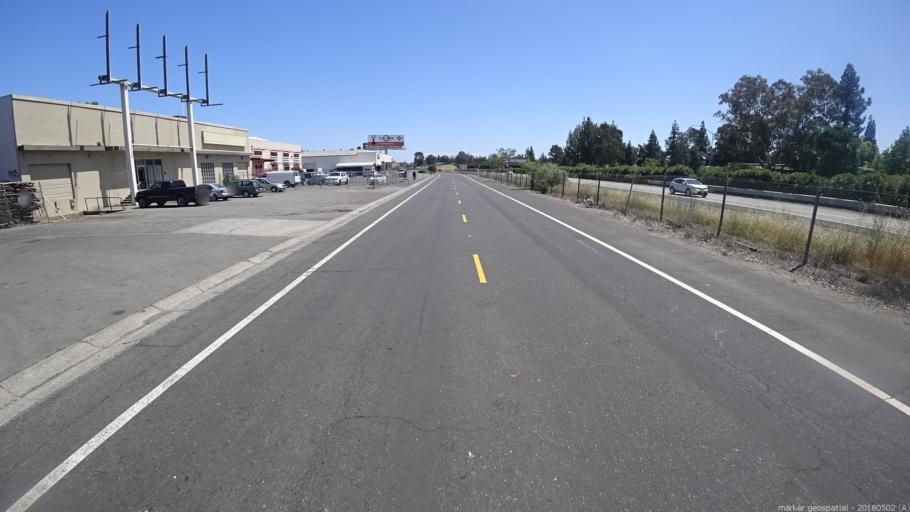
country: US
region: California
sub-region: Sacramento County
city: Sacramento
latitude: 38.6004
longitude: -121.4434
